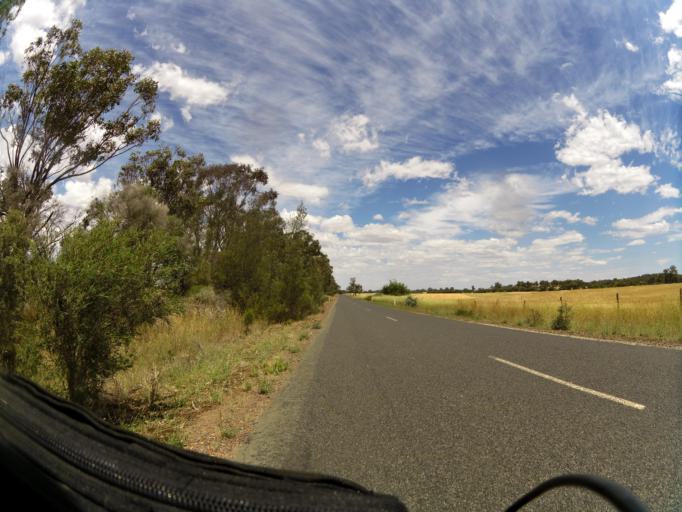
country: AU
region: Victoria
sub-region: Campaspe
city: Kyabram
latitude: -36.7645
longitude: 145.1070
